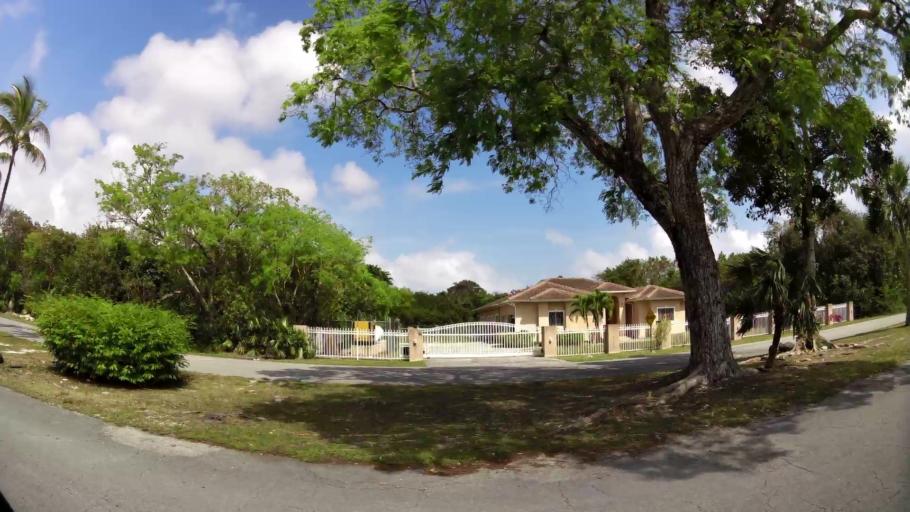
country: BS
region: Freeport
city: Freeport
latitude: 26.5079
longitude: -78.7092
